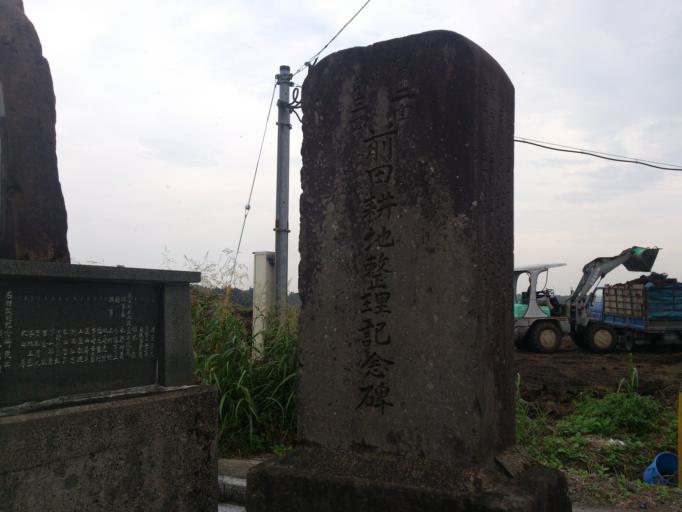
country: JP
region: Kagoshima
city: Kanoya
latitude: 31.3580
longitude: 130.9335
